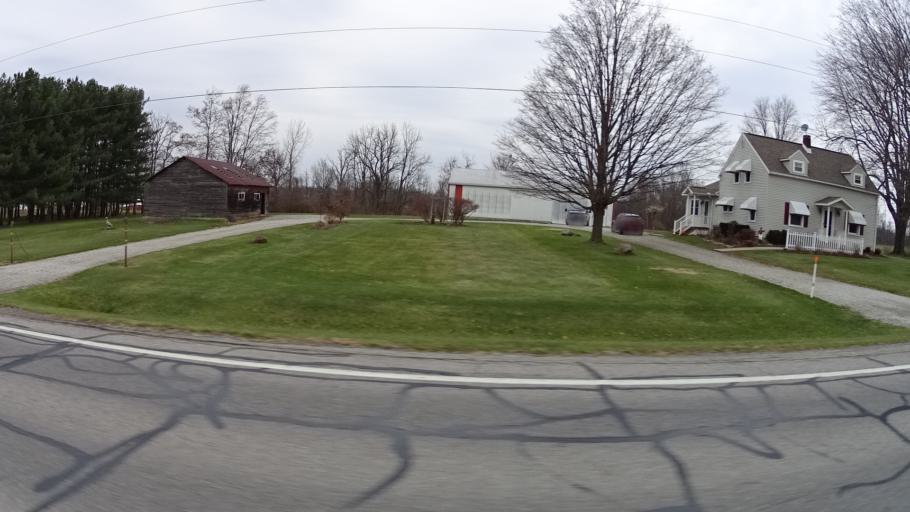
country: US
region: Ohio
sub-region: Lorain County
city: Lagrange
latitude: 41.1682
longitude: -82.0810
